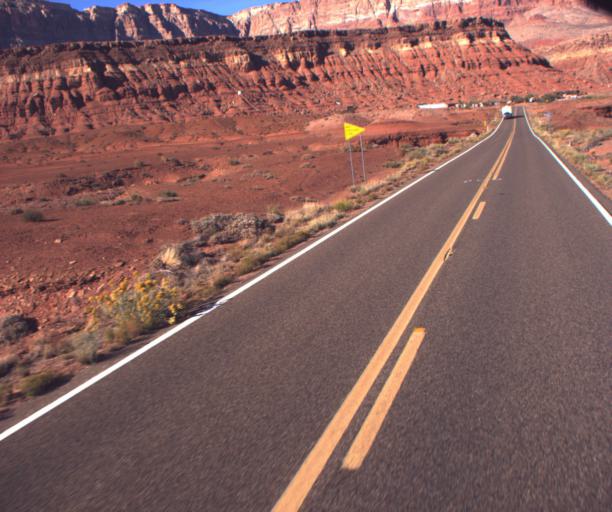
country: US
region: Arizona
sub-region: Coconino County
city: Page
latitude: 36.7363
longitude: -111.7552
